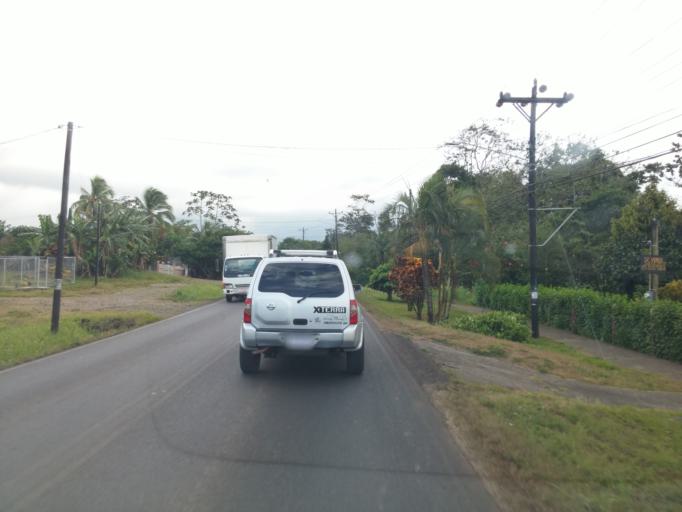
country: CR
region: Alajuela
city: Pital
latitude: 10.3870
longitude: -84.3395
